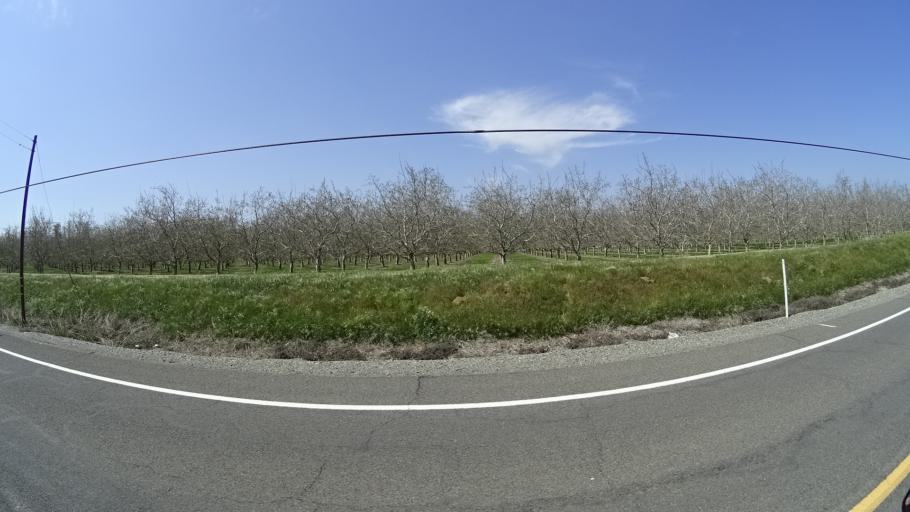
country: US
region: California
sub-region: Glenn County
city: Willows
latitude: 39.4627
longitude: -122.0188
